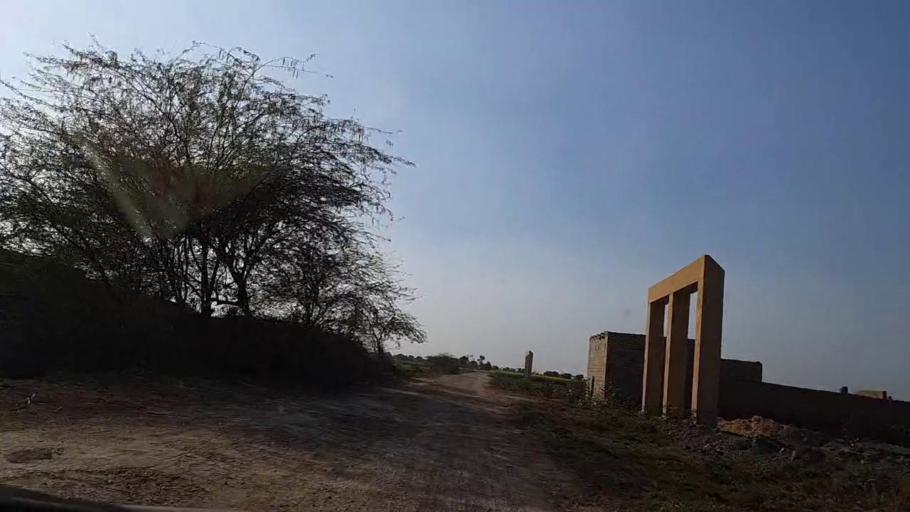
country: PK
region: Sindh
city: Sakrand
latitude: 26.1279
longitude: 68.2670
